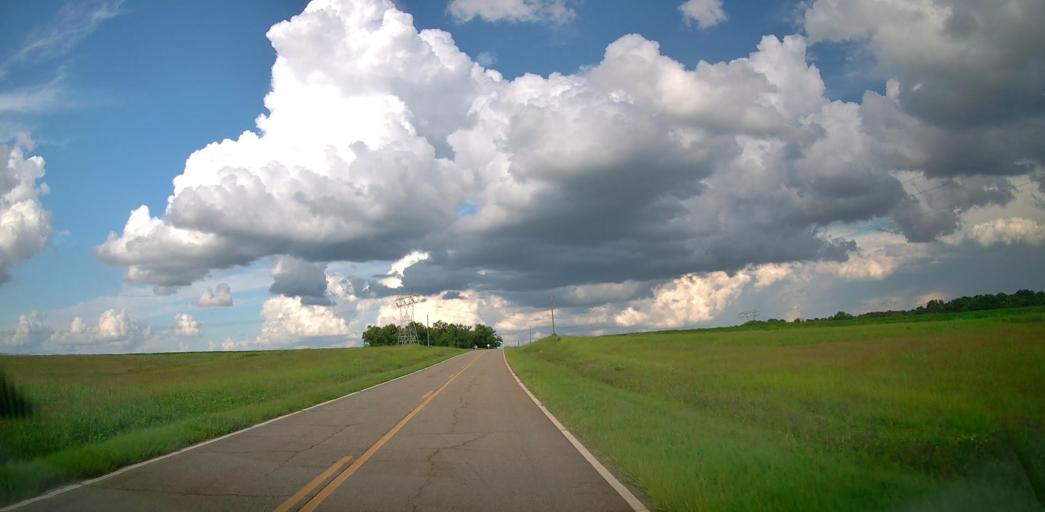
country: US
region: Georgia
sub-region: Bleckley County
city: Cochran
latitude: 32.4062
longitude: -83.4142
